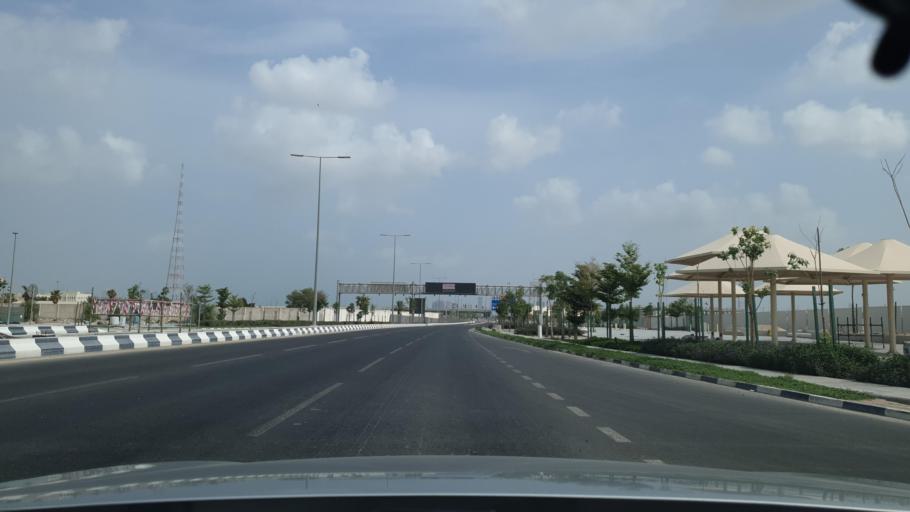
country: QA
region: Baladiyat ar Rayyan
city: Ar Rayyan
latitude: 25.2778
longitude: 51.4633
